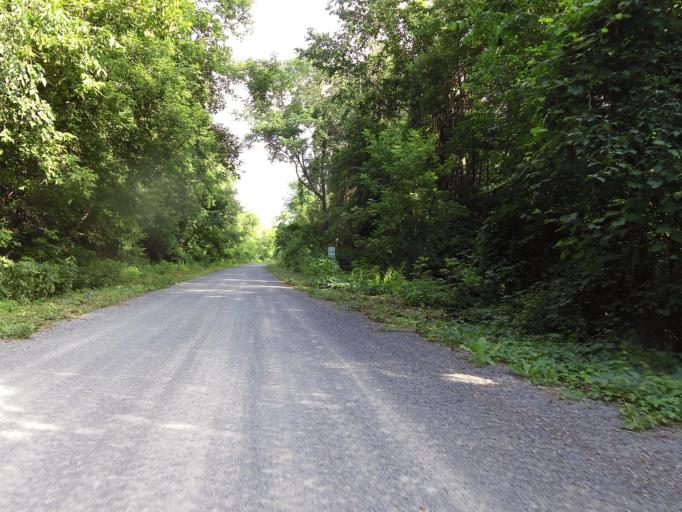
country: CA
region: Ontario
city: Arnprior
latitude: 45.3248
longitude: -76.2881
